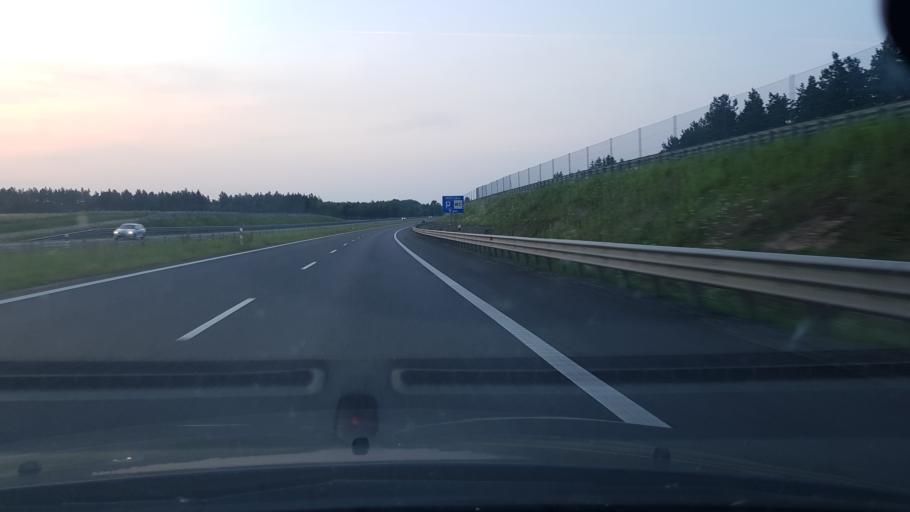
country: PL
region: Warmian-Masurian Voivodeship
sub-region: Powiat olsztynski
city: Olsztynek
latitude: 53.4691
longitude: 20.3212
